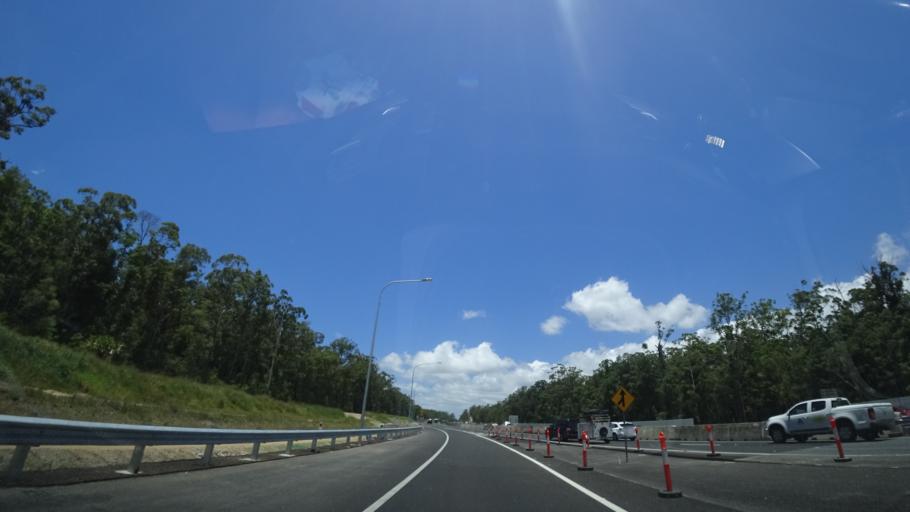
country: AU
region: Queensland
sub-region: Sunshine Coast
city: Little Mountain
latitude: -26.7794
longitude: 153.0440
